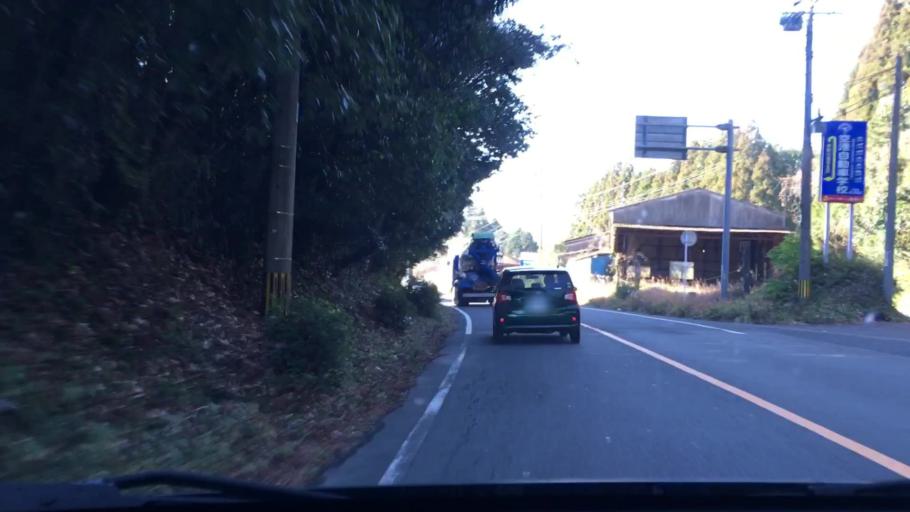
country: JP
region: Kagoshima
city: Kajiki
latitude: 31.7763
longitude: 130.7012
